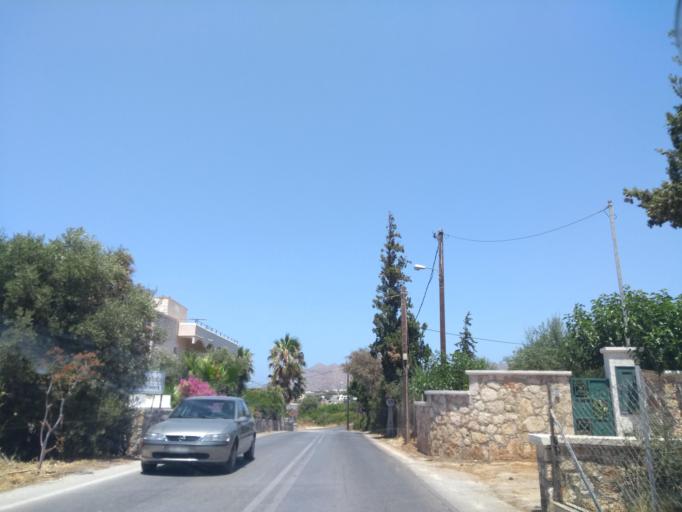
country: GR
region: Crete
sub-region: Nomos Chanias
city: Pithari
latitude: 35.5495
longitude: 24.0841
